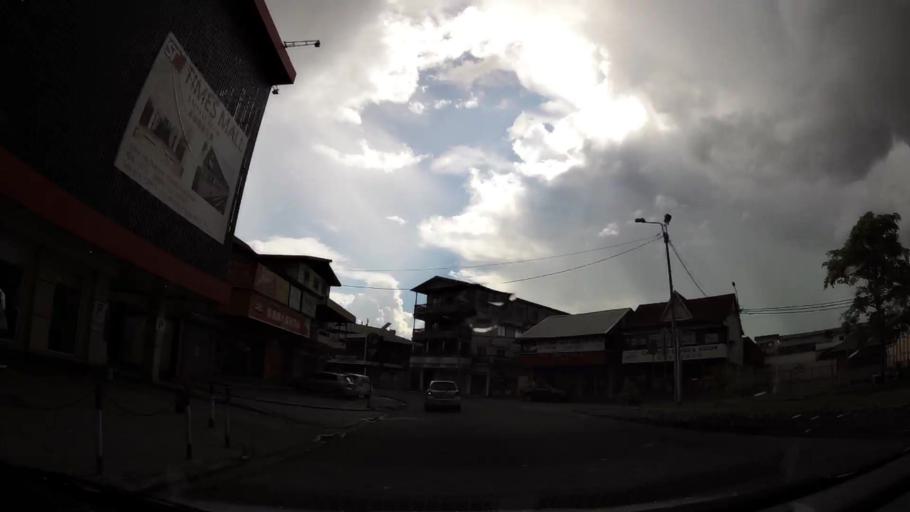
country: SR
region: Paramaribo
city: Paramaribo
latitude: 5.8259
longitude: -55.1621
